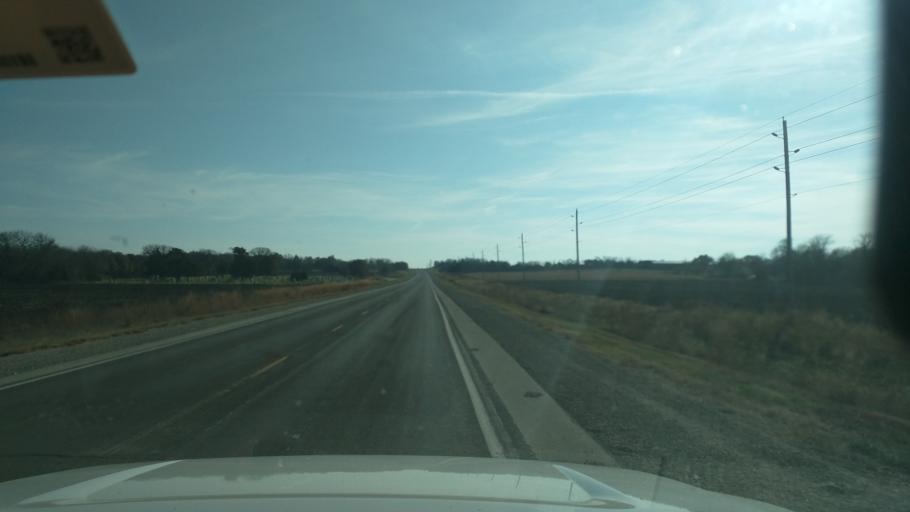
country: US
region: Kansas
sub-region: Lyon County
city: Emporia
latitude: 38.3603
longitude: -96.1805
